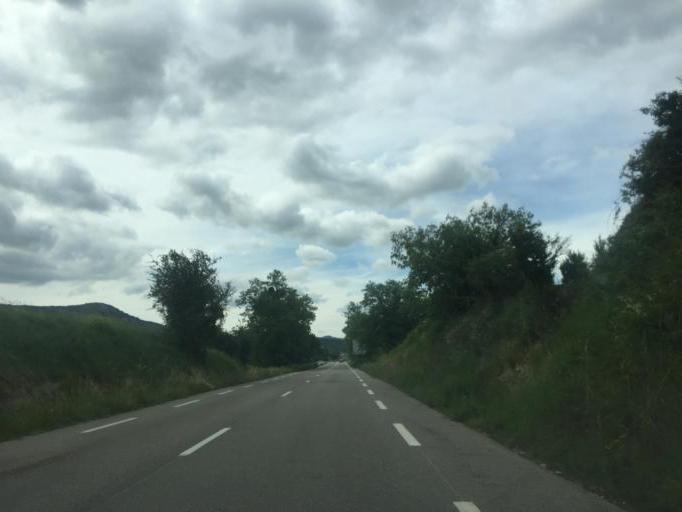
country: FR
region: Rhone-Alpes
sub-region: Departement de l'Ardeche
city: Alba-la-Romaine
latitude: 44.5597
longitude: 4.5998
